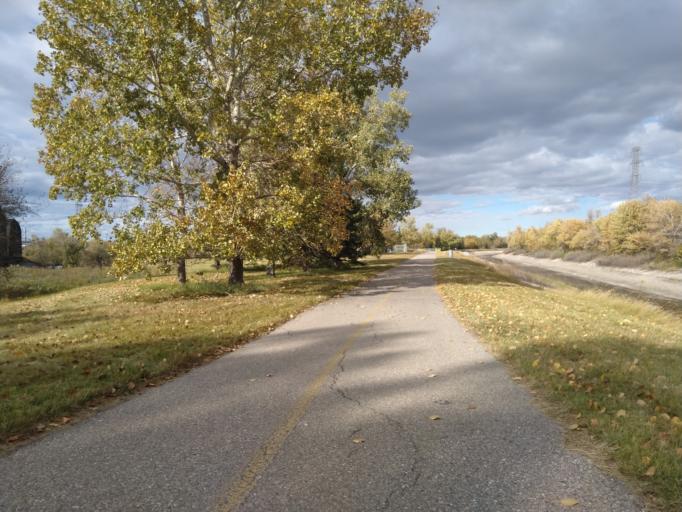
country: CA
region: Alberta
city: Calgary
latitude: 51.0151
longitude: -114.0100
